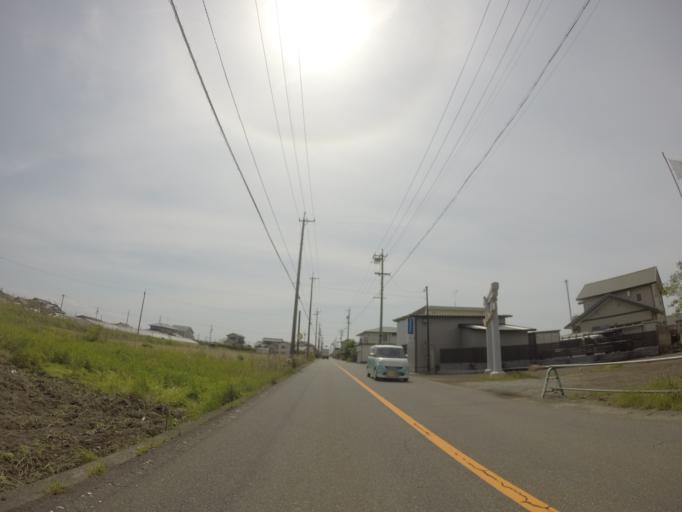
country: JP
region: Shizuoka
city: Fujieda
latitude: 34.8101
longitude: 138.2849
